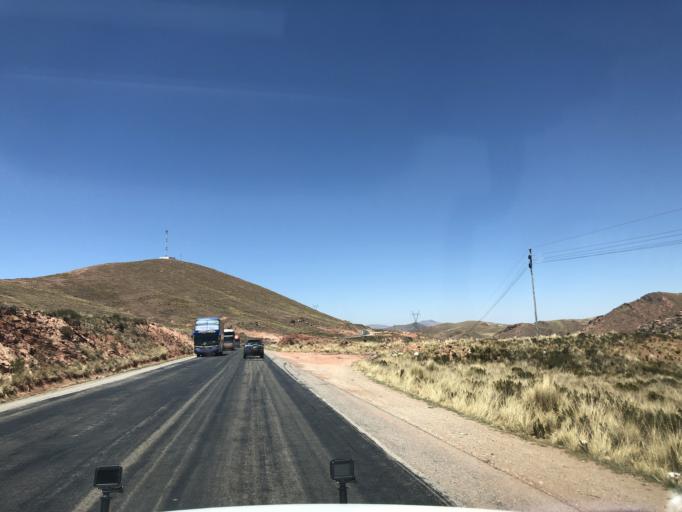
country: BO
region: Cochabamba
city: Colchani
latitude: -17.6933
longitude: -66.7021
